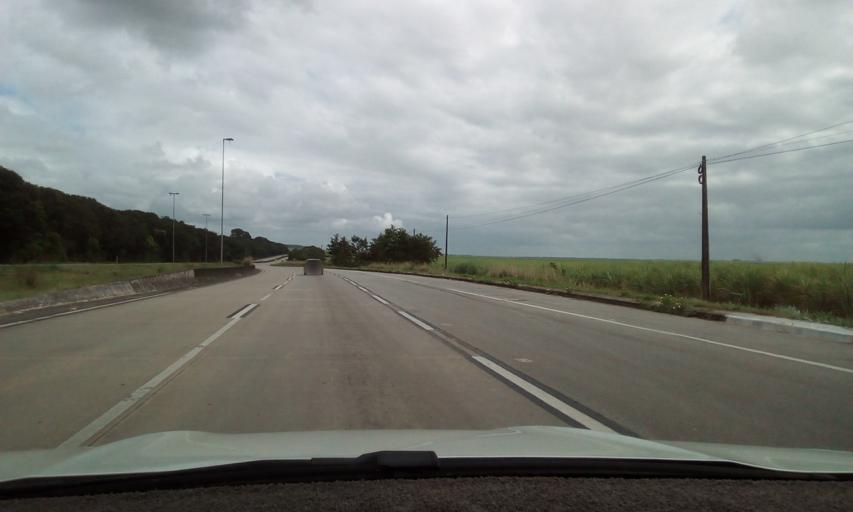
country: BR
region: Paraiba
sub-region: Santa Rita
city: Santa Rita
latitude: -7.0792
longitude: -34.9863
